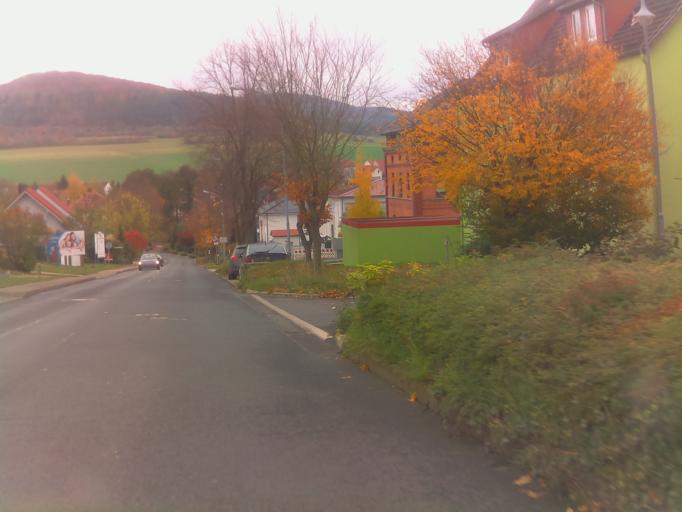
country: DE
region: Thuringia
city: Geisa
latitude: 50.7191
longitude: 9.9449
